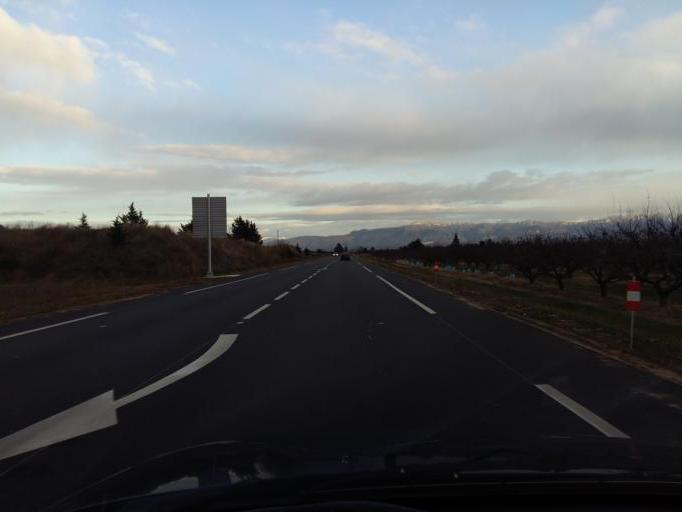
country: FR
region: Rhone-Alpes
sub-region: Departement de la Drome
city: Clerieux
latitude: 45.0478
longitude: 4.9979
